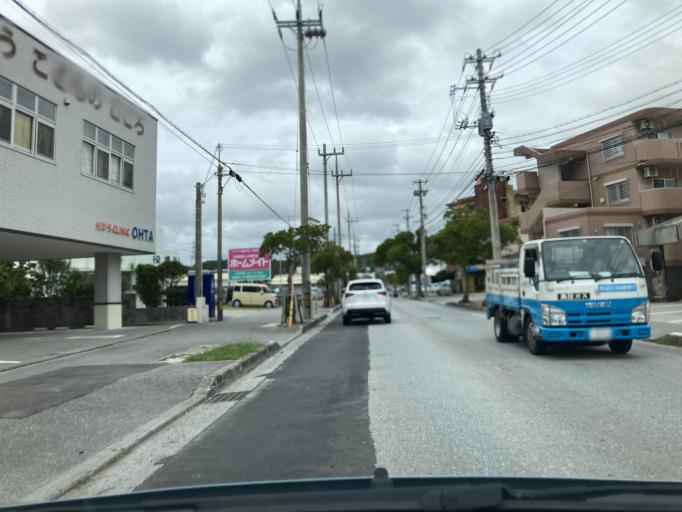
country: JP
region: Okinawa
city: Ginowan
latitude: 26.2262
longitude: 127.7640
